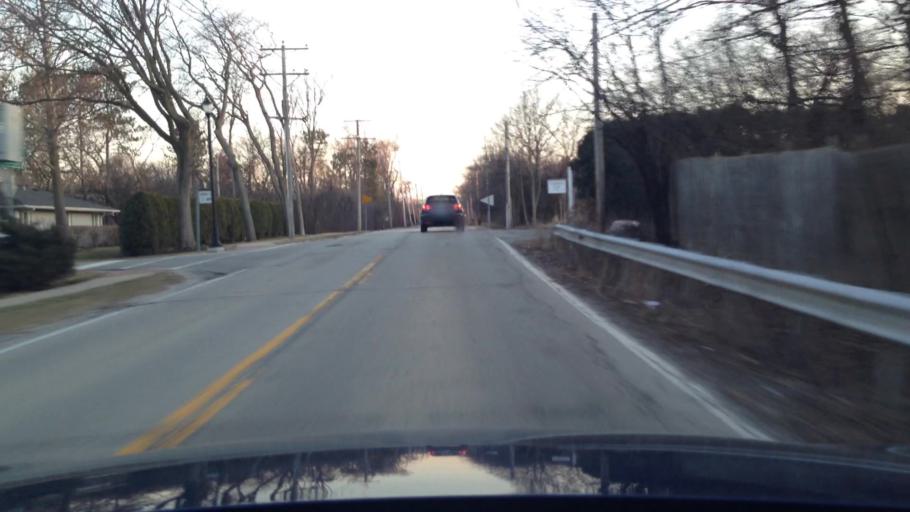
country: US
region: Illinois
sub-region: Cook County
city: Northfield
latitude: 42.1161
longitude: -87.7901
